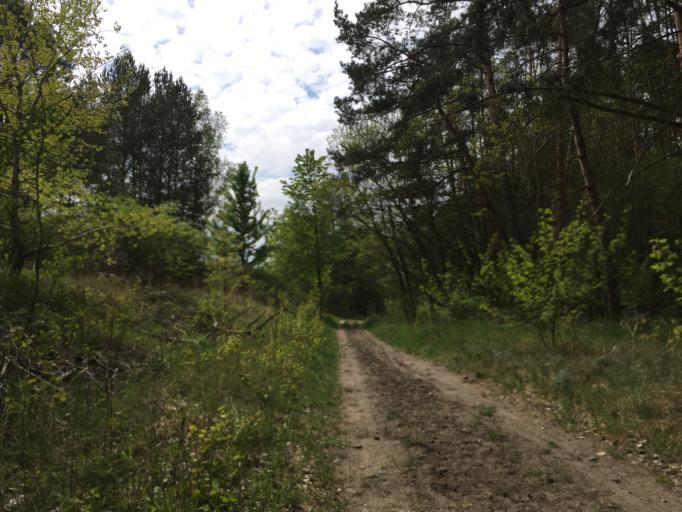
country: DE
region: Brandenburg
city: Rudnitz
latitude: 52.7097
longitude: 13.6275
